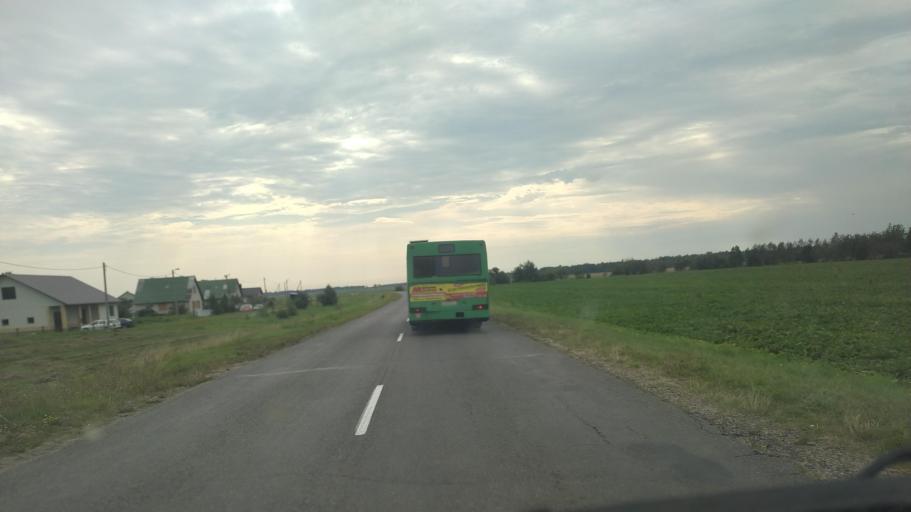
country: BY
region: Brest
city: Byaroza
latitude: 52.5778
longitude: 24.8578
